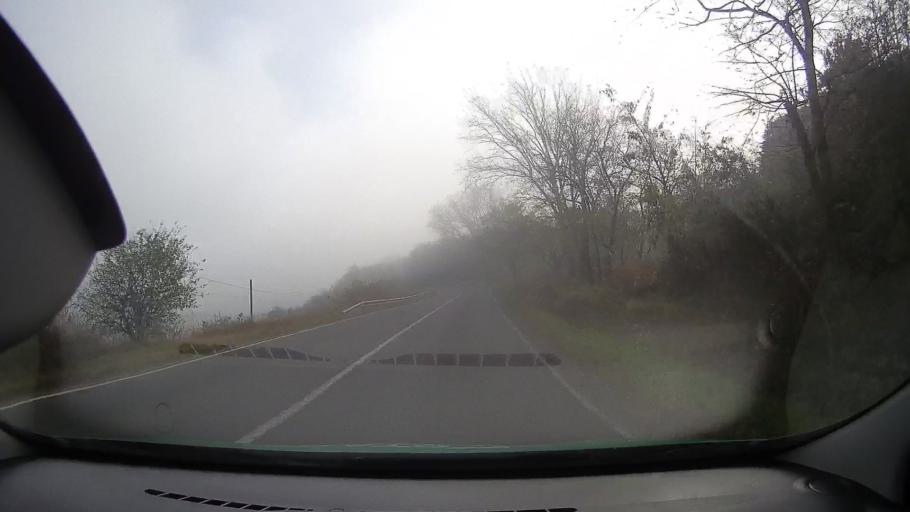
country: RO
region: Tulcea
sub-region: Municipiul Tulcea
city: Tulcea
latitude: 45.1673
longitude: 28.8373
